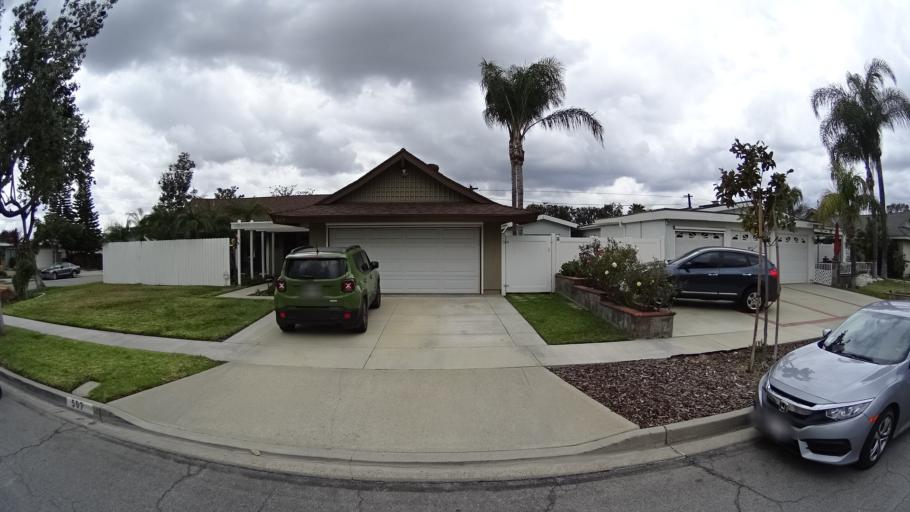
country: US
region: California
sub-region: Orange County
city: Placentia
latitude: 33.8460
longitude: -117.8730
